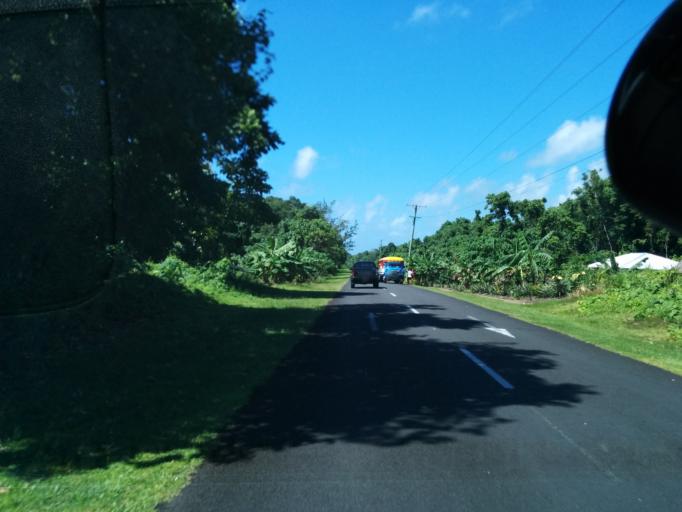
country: WS
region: Fa`asaleleaga
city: Safotulafai
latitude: -13.5355
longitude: -172.2529
